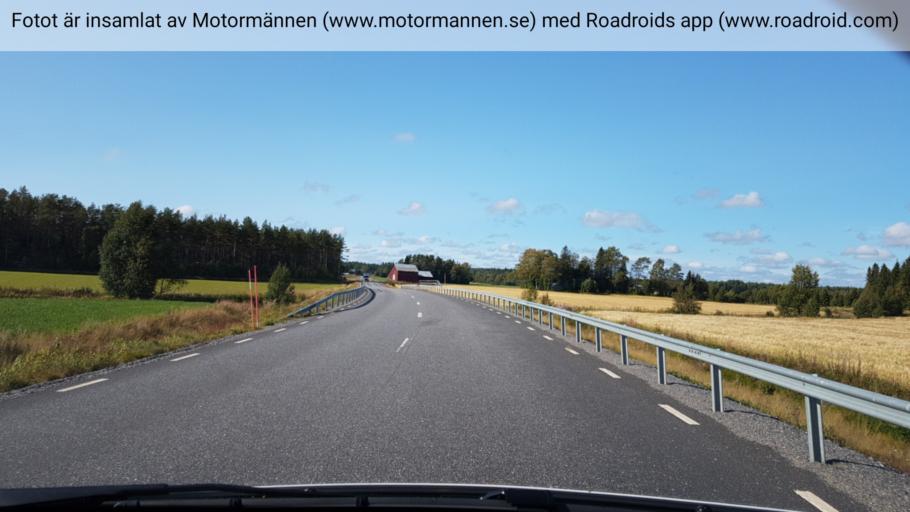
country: SE
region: Vaesterbotten
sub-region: Robertsfors Kommun
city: Robertsfors
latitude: 64.2328
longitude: 20.9702
